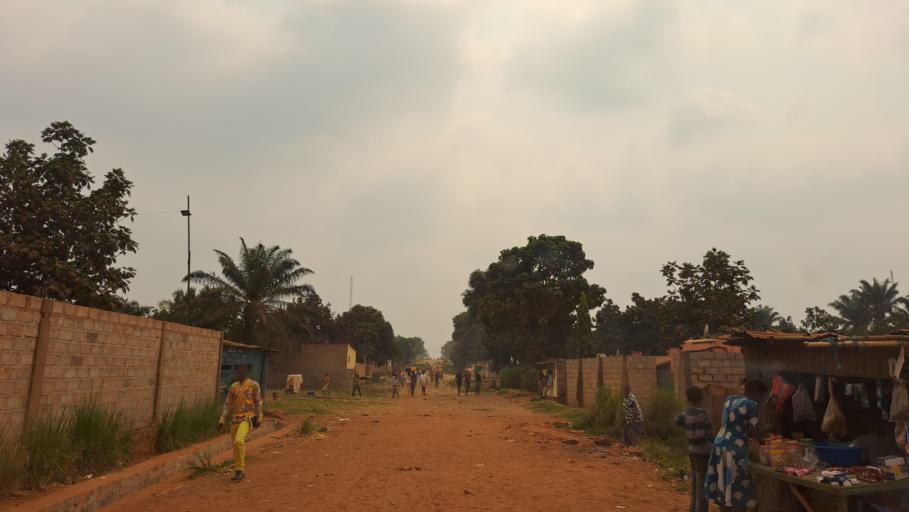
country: CD
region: Kasai-Oriental
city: Mbuji-Mayi
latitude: -6.1127
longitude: 23.5986
